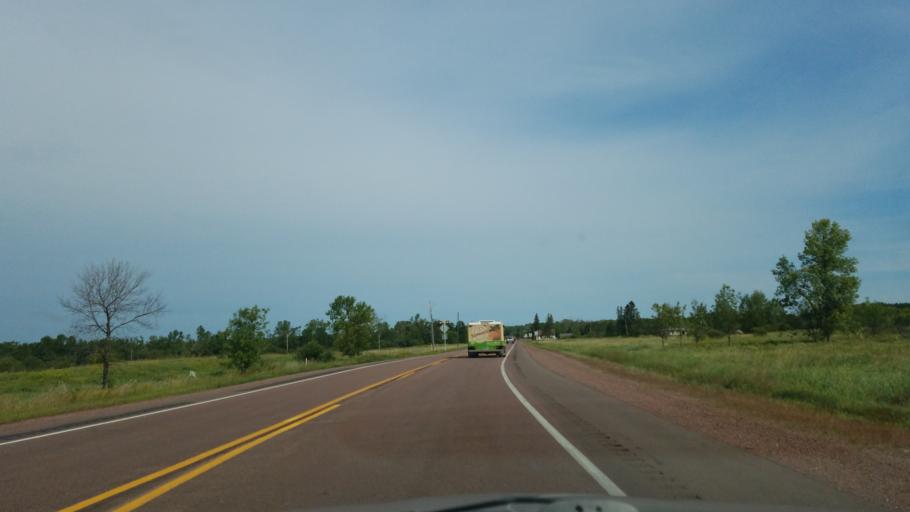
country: US
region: Wisconsin
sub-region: Ashland County
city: Ashland
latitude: 46.5896
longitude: -90.9551
